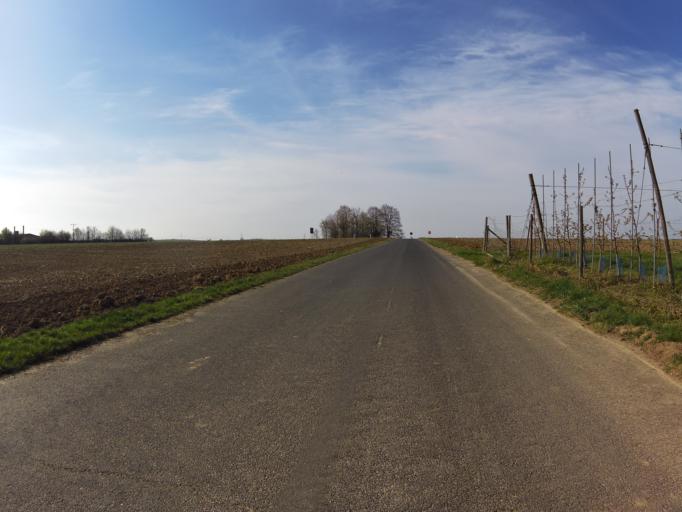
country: DE
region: Bavaria
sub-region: Regierungsbezirk Unterfranken
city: Biebelried
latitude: 49.7892
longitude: 10.1122
